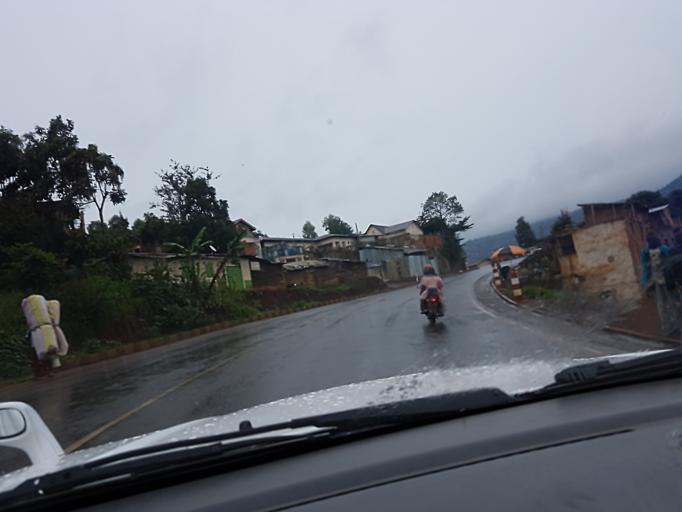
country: CD
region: South Kivu
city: Bukavu
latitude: -2.5066
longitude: 28.8554
